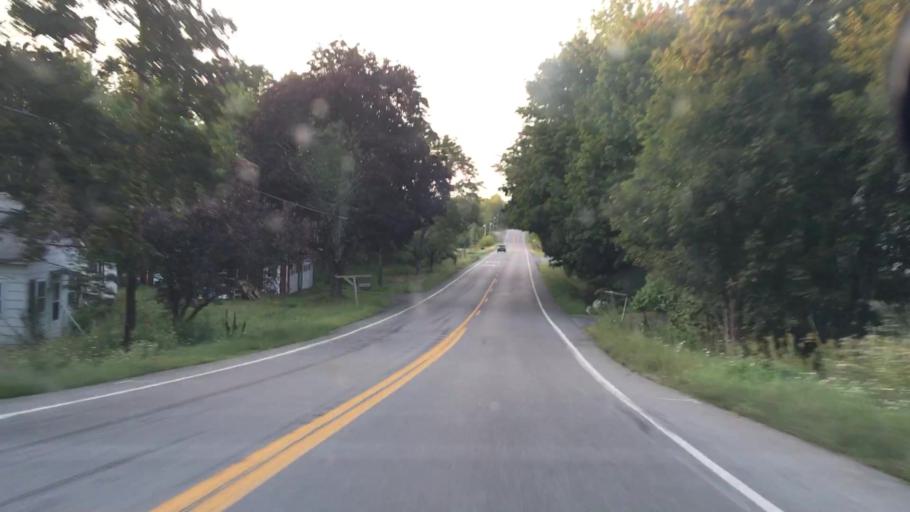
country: US
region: Maine
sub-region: Penobscot County
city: Hermon
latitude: 44.7353
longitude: -68.9640
